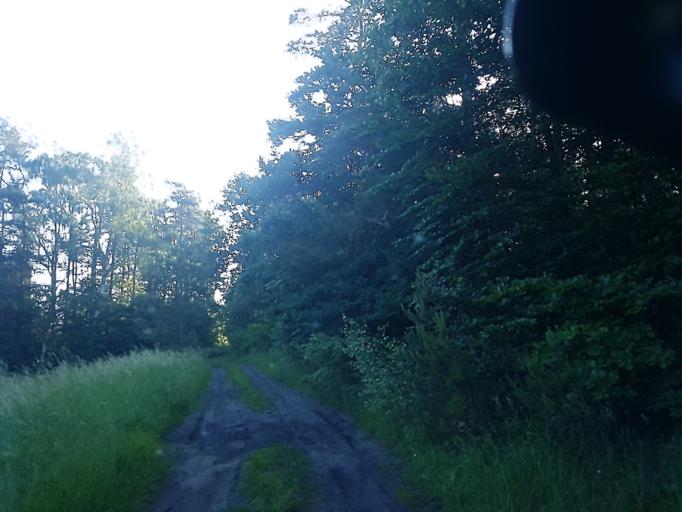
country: DE
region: Brandenburg
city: Schonborn
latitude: 51.5997
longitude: 13.4748
